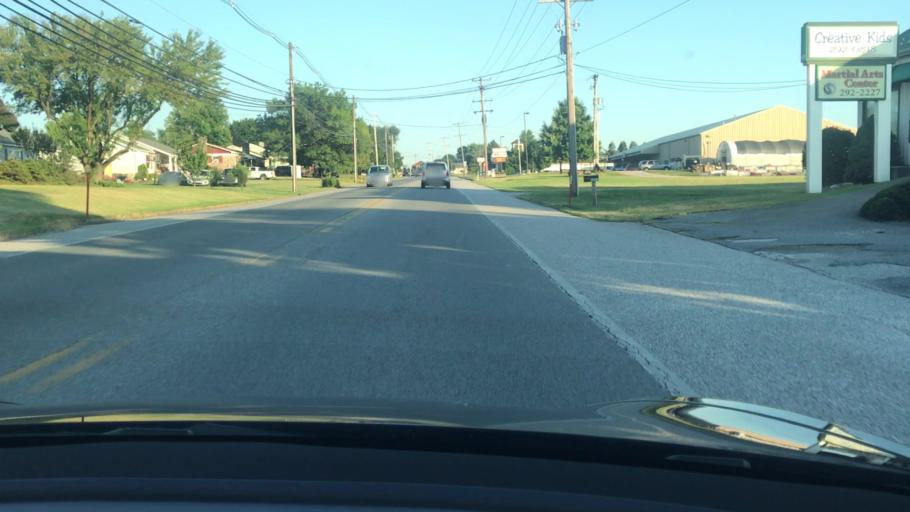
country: US
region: Pennsylvania
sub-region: York County
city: Dover
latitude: 39.9967
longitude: -76.8452
